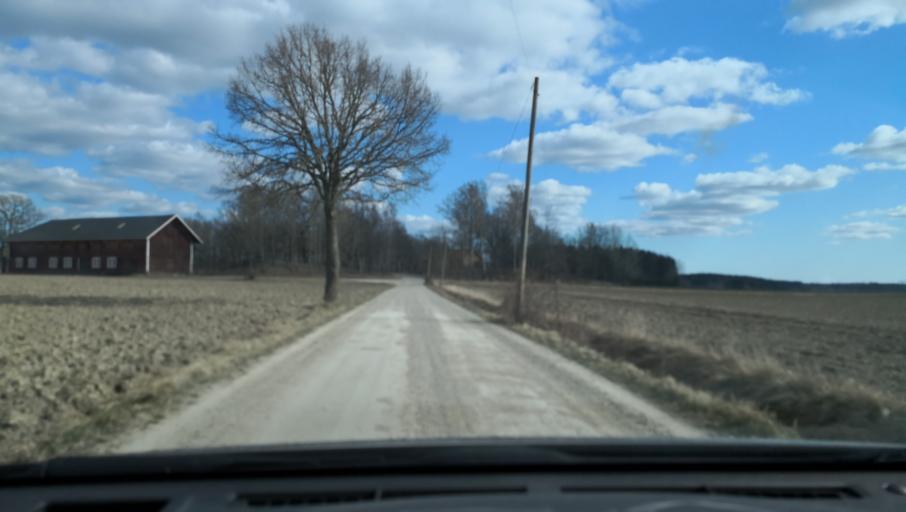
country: SE
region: Soedermanland
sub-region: Katrineholms Kommun
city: Katrineholm
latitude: 59.1426
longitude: 16.0782
